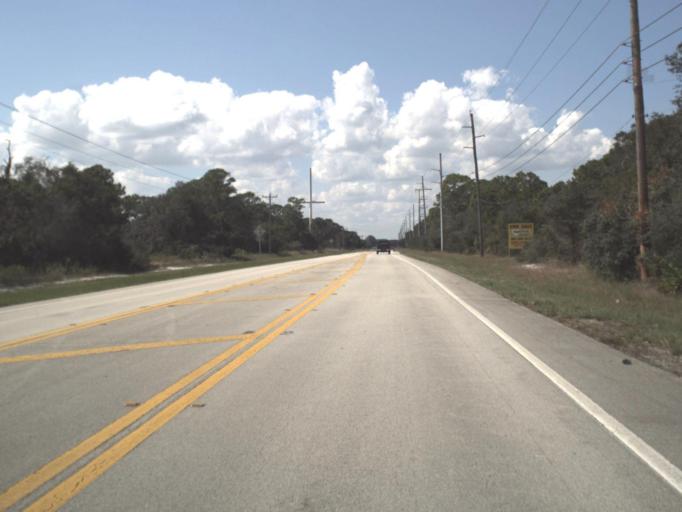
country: US
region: Florida
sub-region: Highlands County
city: Sebring
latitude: 27.4404
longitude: -81.3044
